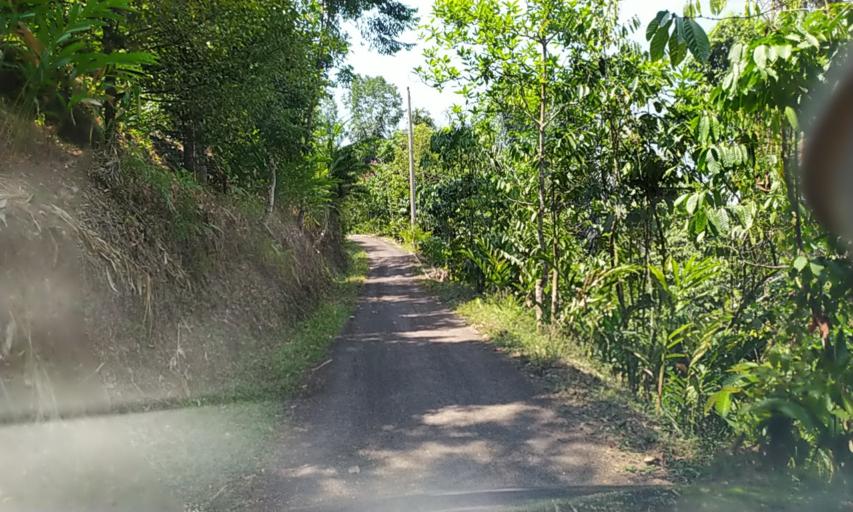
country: ID
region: Central Java
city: Kaduluhur
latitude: -7.1780
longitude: 108.6392
